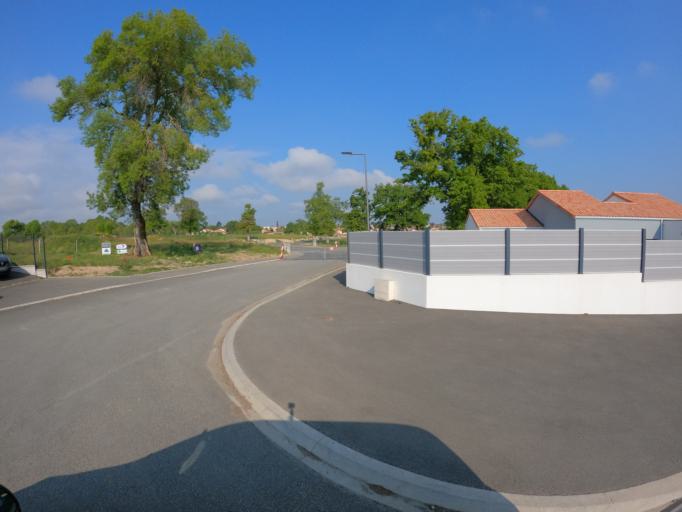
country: FR
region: Pays de la Loire
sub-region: Departement de Maine-et-Loire
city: La Romagne
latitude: 47.0571
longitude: -1.0182
